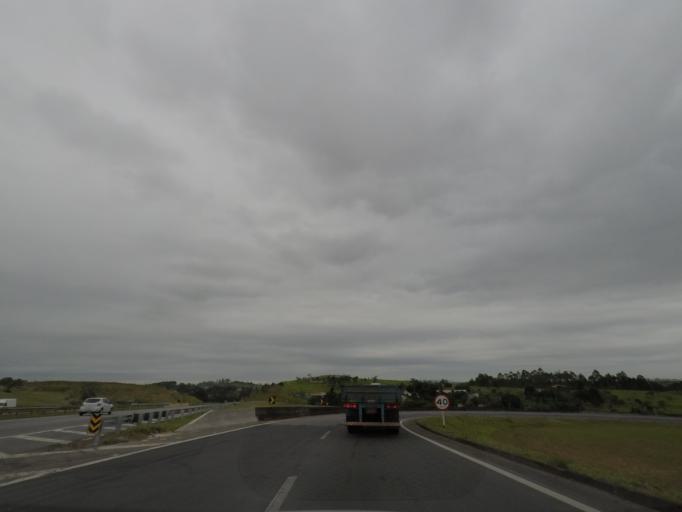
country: BR
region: Sao Paulo
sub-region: Jacarei
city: Jacarei
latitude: -23.3086
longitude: -46.0451
